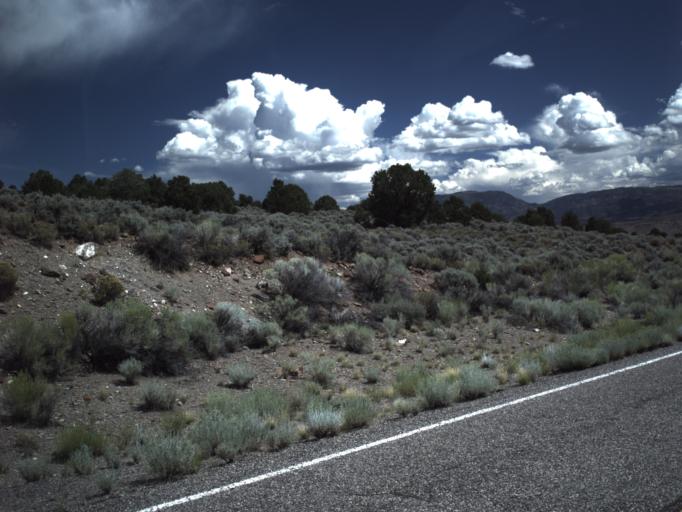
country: US
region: Utah
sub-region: Piute County
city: Junction
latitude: 38.2604
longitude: -112.2582
